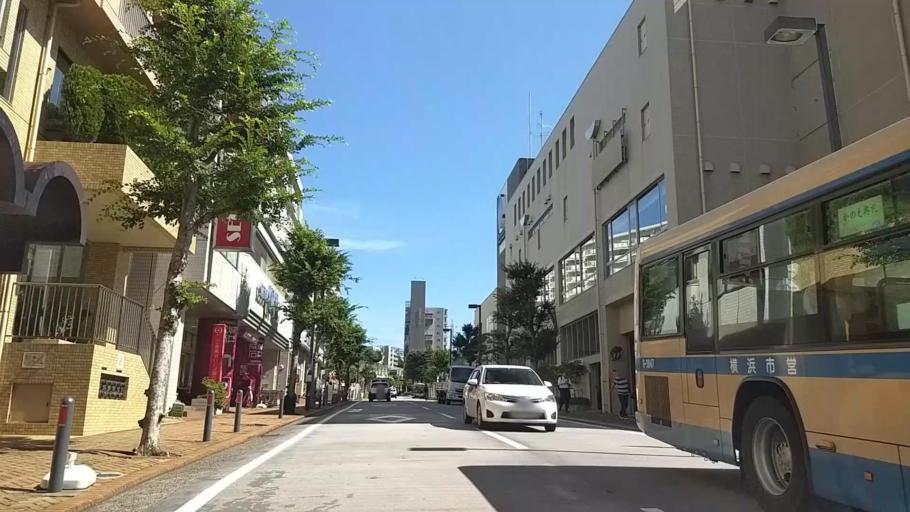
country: JP
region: Tokyo
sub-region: Machida-shi
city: Machida
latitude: 35.5507
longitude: 139.5400
